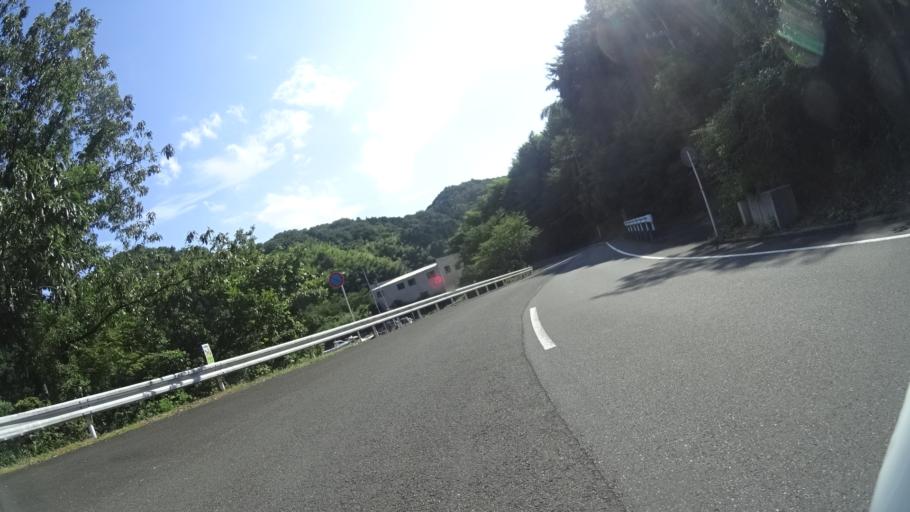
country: JP
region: Kyoto
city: Maizuru
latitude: 35.4775
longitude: 135.3169
